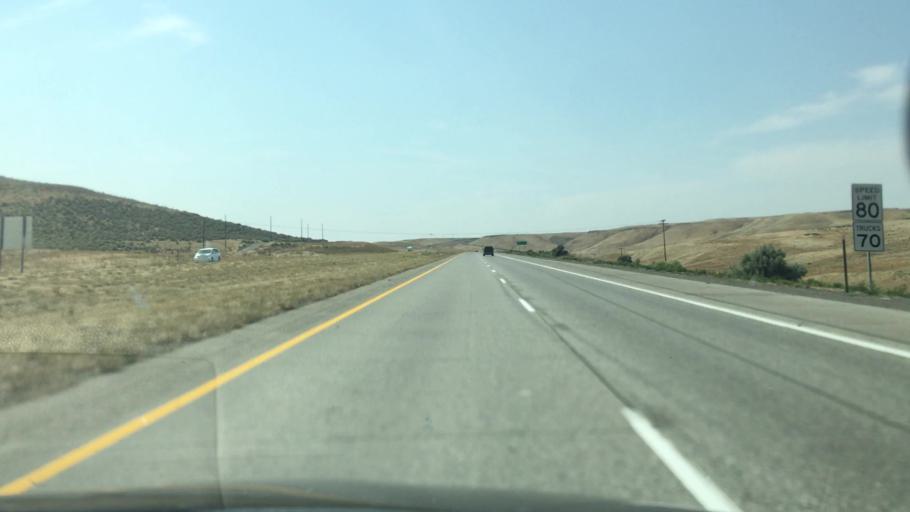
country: US
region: Idaho
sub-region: Elmore County
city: Glenns Ferry
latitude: 42.9633
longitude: -115.3203
